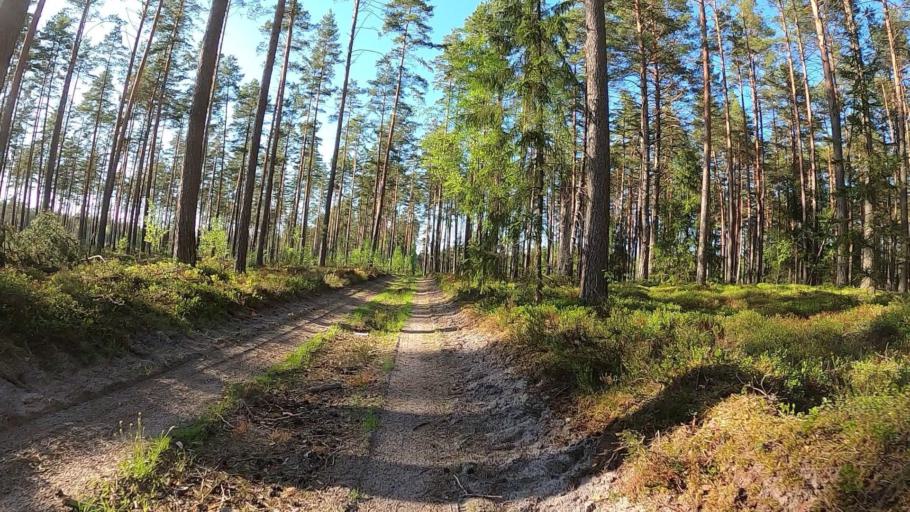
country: LV
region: Baldone
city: Baldone
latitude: 56.7678
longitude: 24.3631
